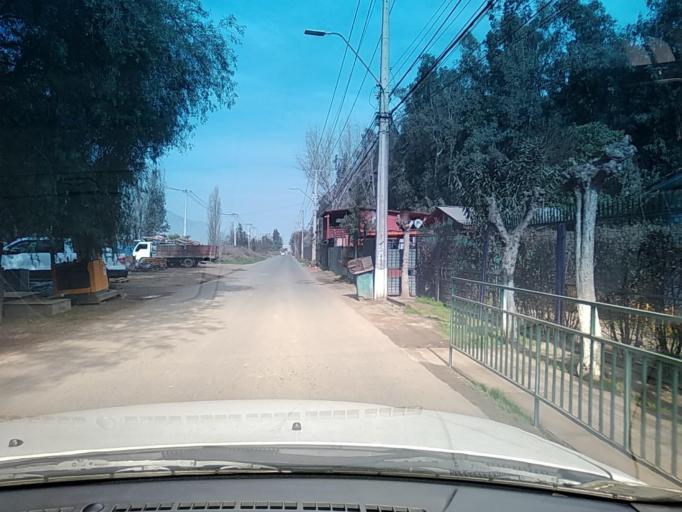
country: CL
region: Santiago Metropolitan
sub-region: Provincia de Chacabuco
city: Chicureo Abajo
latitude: -33.2920
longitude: -70.7258
